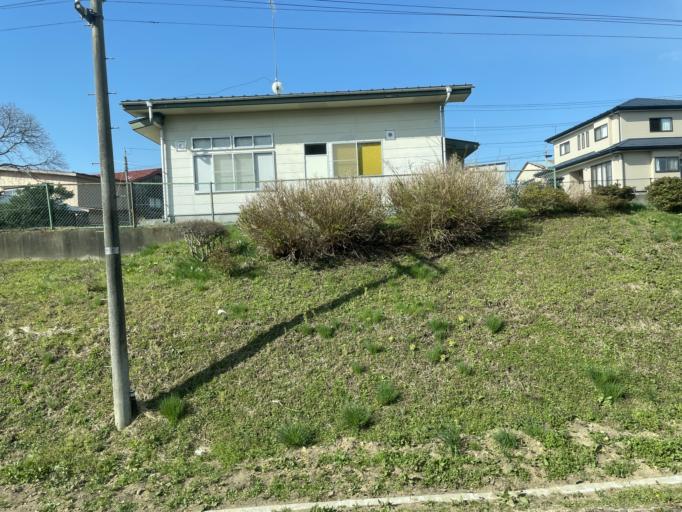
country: JP
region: Aomori
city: Hachinohe
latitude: 40.4562
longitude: 141.6657
